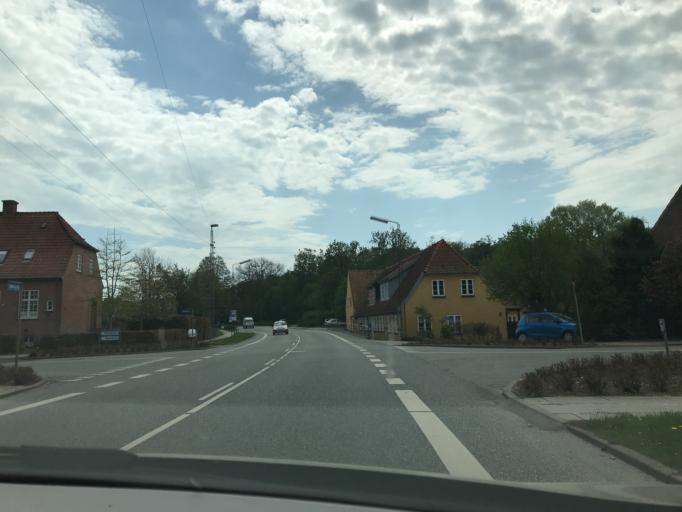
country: DK
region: South Denmark
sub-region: Assens Kommune
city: Assens
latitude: 55.2675
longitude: 9.9015
